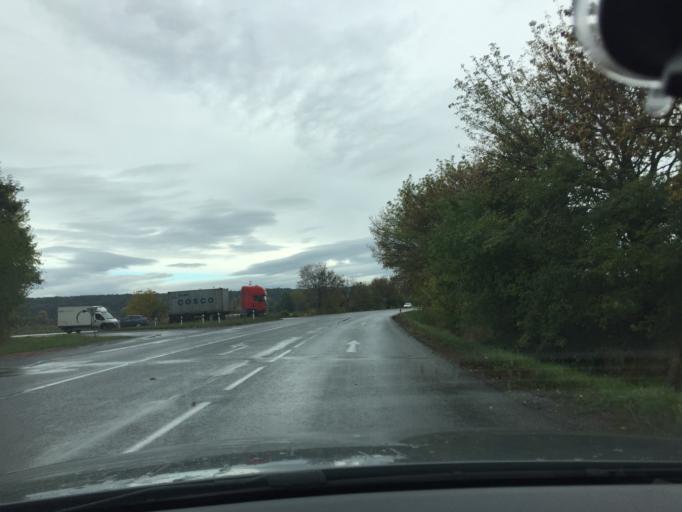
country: CZ
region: Central Bohemia
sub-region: Okres Melnik
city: Veltrusy
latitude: 50.2665
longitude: 14.3231
